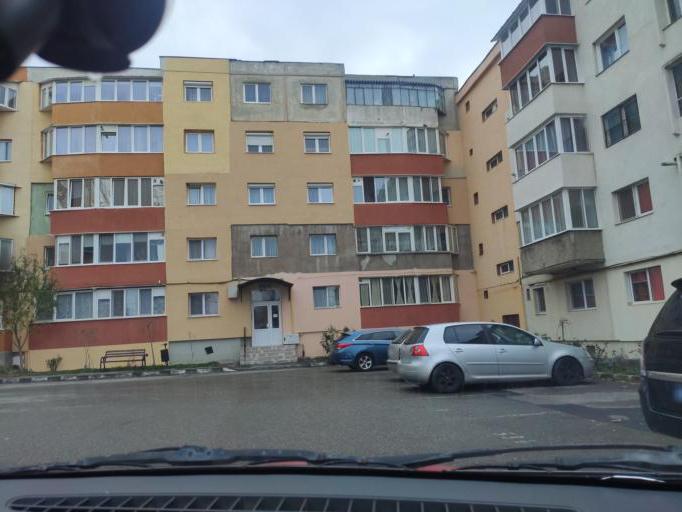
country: RO
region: Brasov
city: Codlea
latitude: 45.7027
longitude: 25.4454
